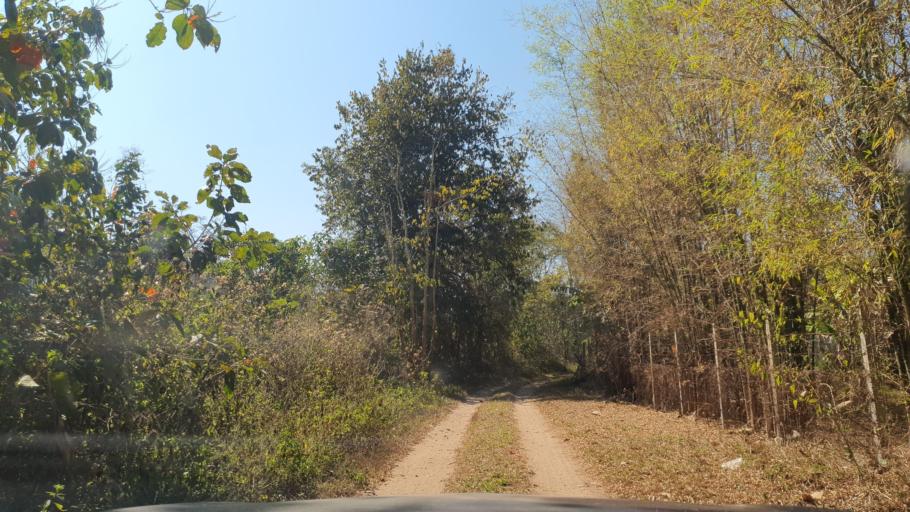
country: TH
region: Chiang Mai
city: Mae On
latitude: 18.8725
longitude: 99.2611
